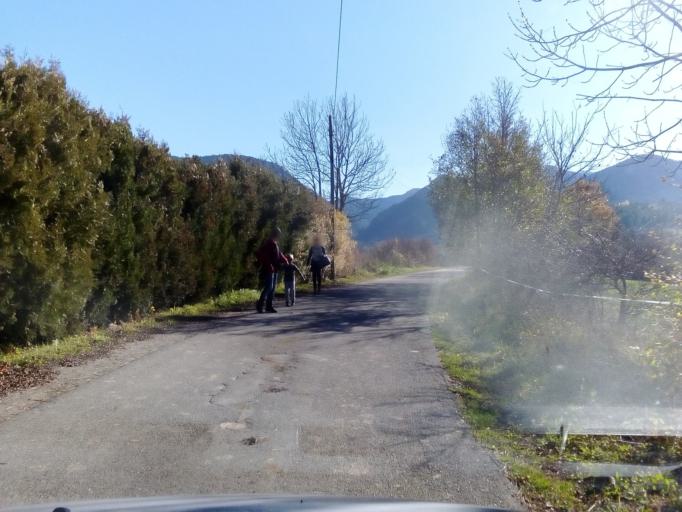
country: ES
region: Catalonia
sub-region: Provincia de Lleida
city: Bellver de Cerdanya
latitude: 42.3592
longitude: 1.7811
